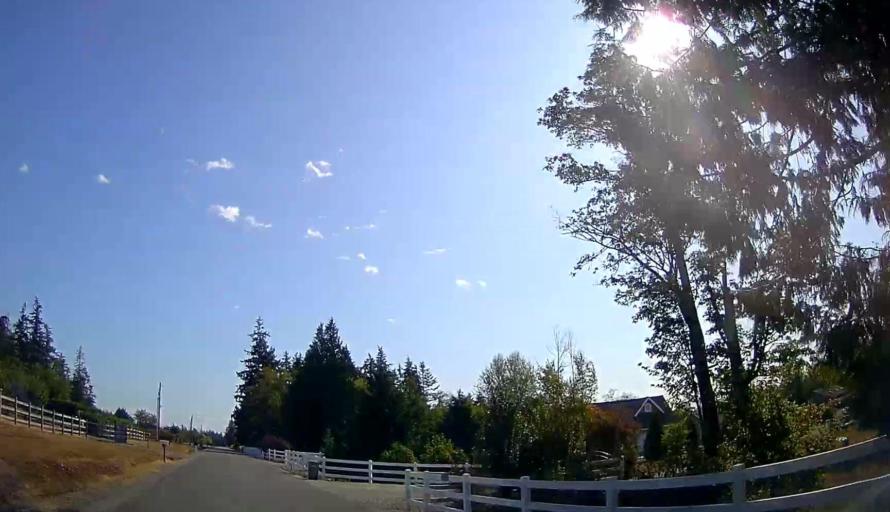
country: US
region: Washington
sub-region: Skagit County
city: Burlington
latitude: 48.4938
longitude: -122.4641
